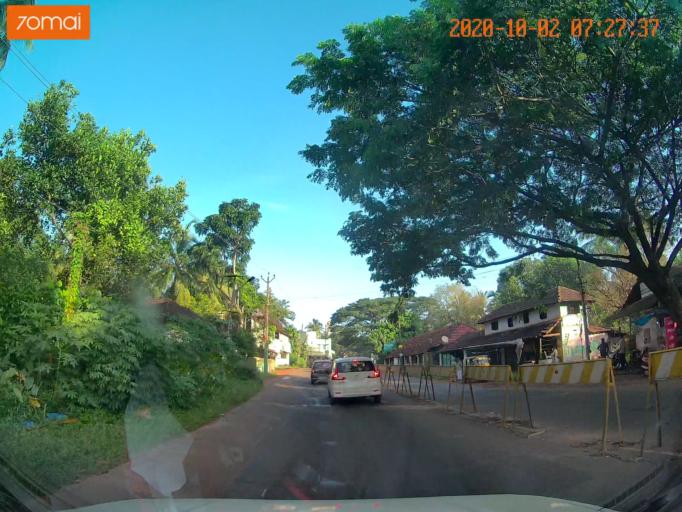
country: IN
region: Kerala
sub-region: Malappuram
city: Pariyapuram
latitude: 11.0258
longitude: 75.9473
